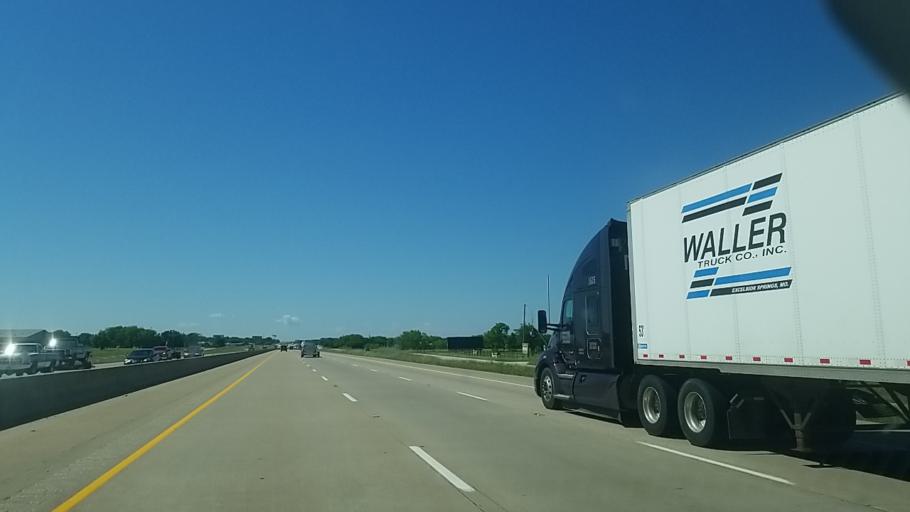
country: US
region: Texas
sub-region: Navarro County
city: Corsicana
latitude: 32.2268
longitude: -96.4874
